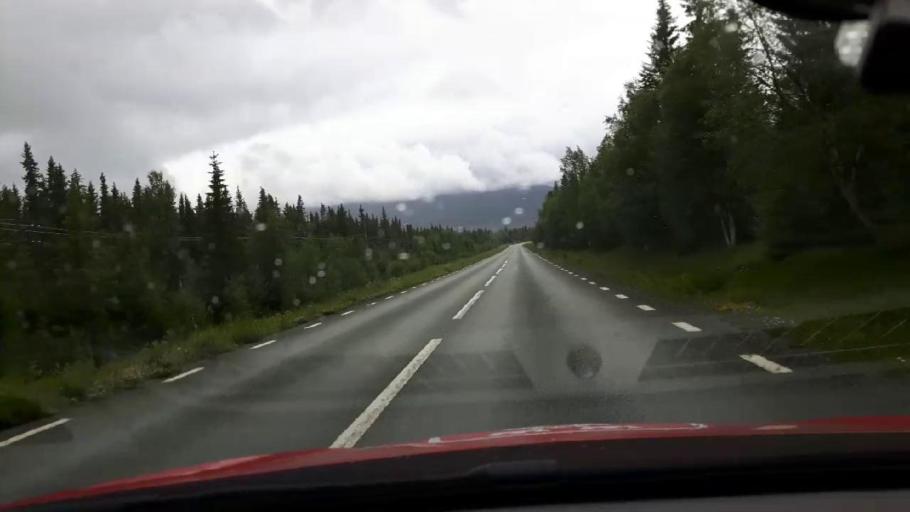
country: NO
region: Nord-Trondelag
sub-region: Meraker
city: Meraker
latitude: 63.2952
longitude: 12.4084
